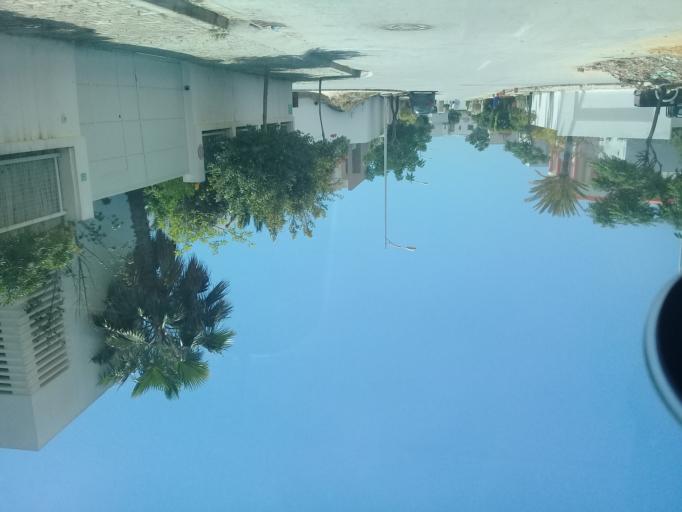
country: TN
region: Tunis
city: La Goulette
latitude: 36.8433
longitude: 10.2680
